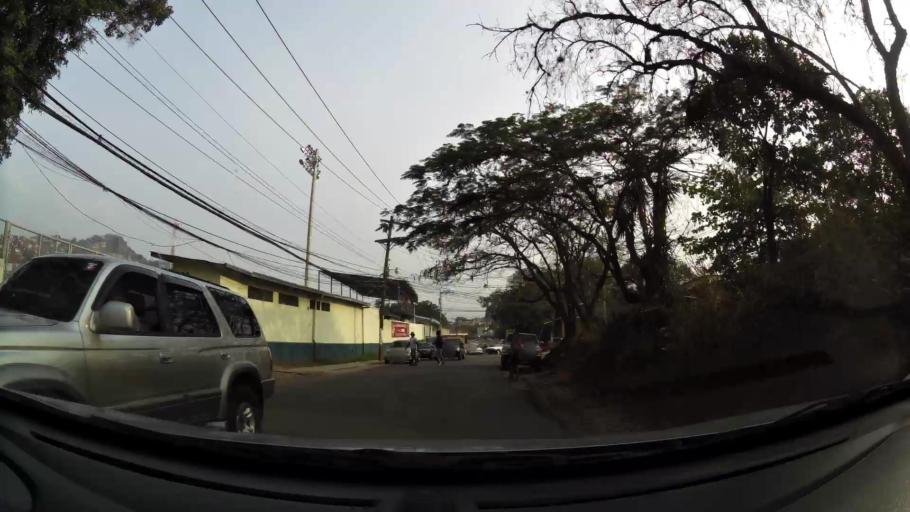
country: HN
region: Francisco Morazan
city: El Tablon
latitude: 14.0662
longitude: -87.1758
